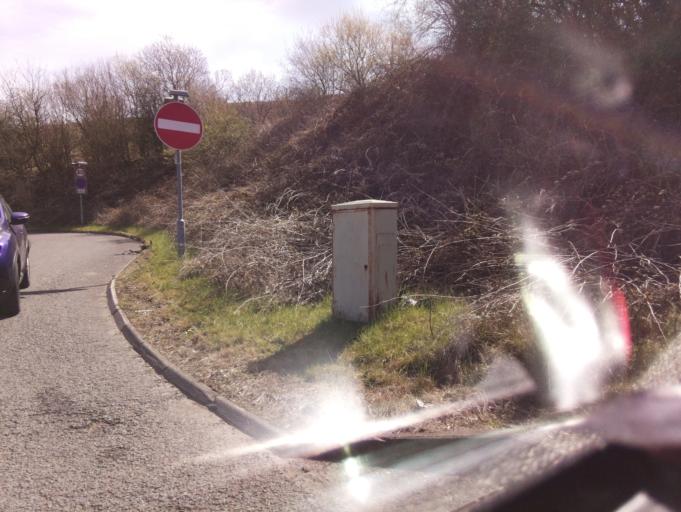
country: GB
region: Wales
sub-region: Rhondda Cynon Taf
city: Aberdare
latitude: 51.7557
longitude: -3.4276
